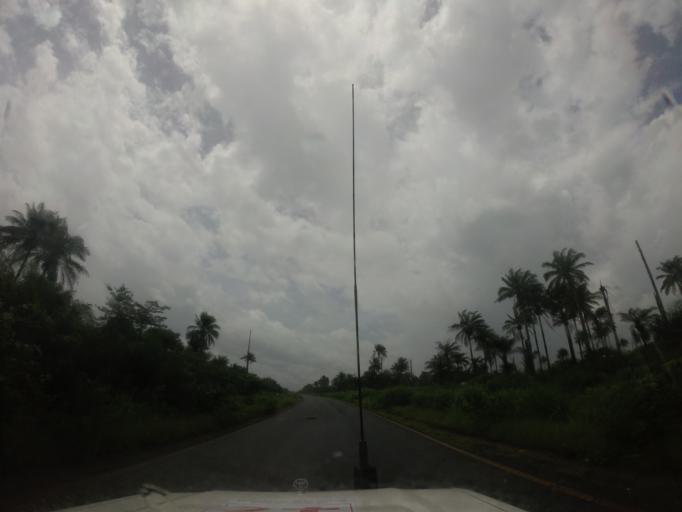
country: SL
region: Northern Province
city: Port Loko
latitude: 8.4857
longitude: -12.7902
